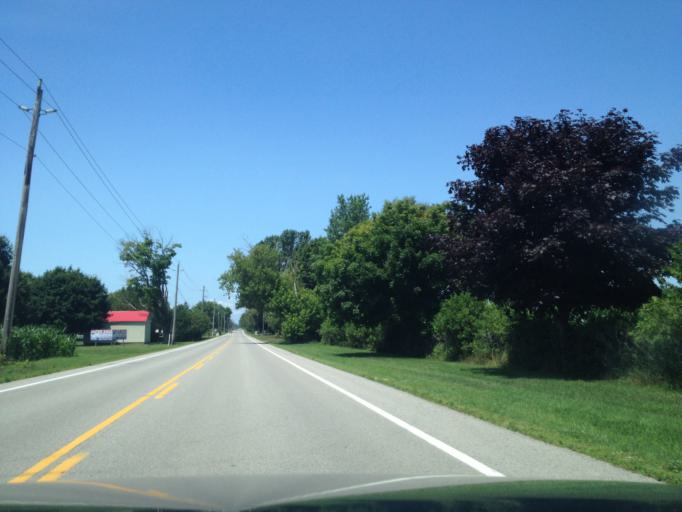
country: CA
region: Ontario
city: Norfolk County
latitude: 42.5982
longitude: -80.6534
